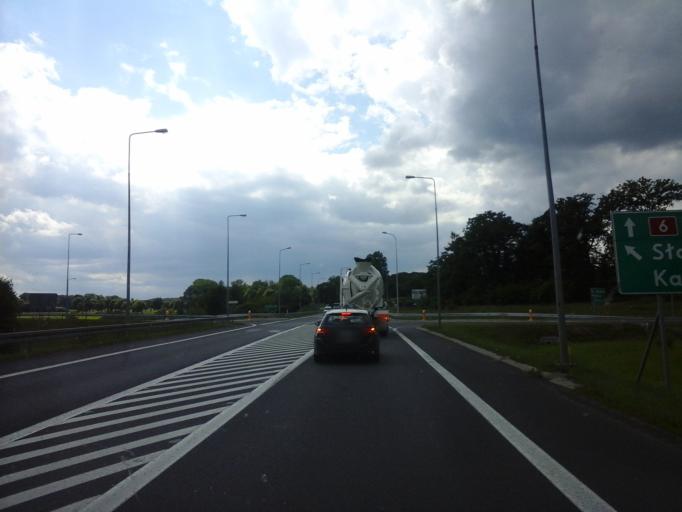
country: PL
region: West Pomeranian Voivodeship
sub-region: Powiat bialogardzki
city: Karlino
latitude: 54.0262
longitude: 15.8631
